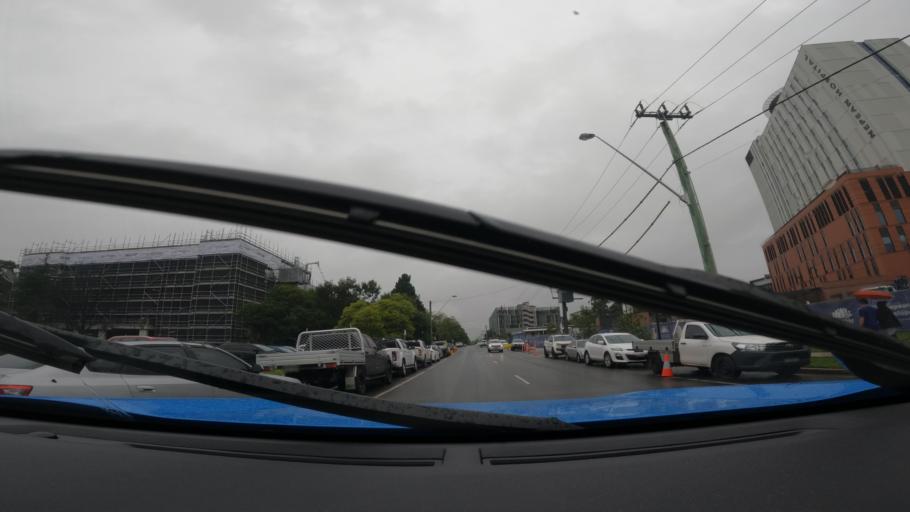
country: AU
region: New South Wales
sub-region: Penrith Municipality
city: Kingswood Park
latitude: -33.7591
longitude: 150.7161
